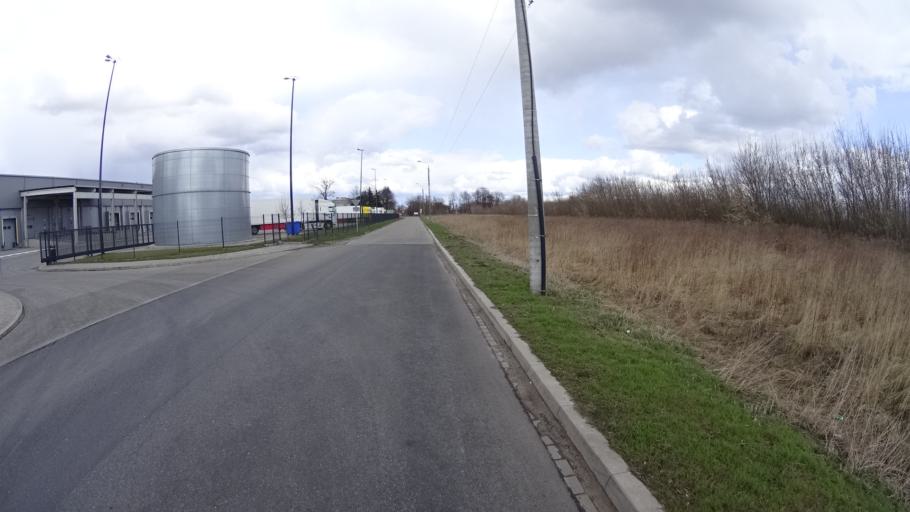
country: PL
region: Masovian Voivodeship
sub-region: Powiat warszawski zachodni
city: Jozefow
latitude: 52.2132
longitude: 20.7151
